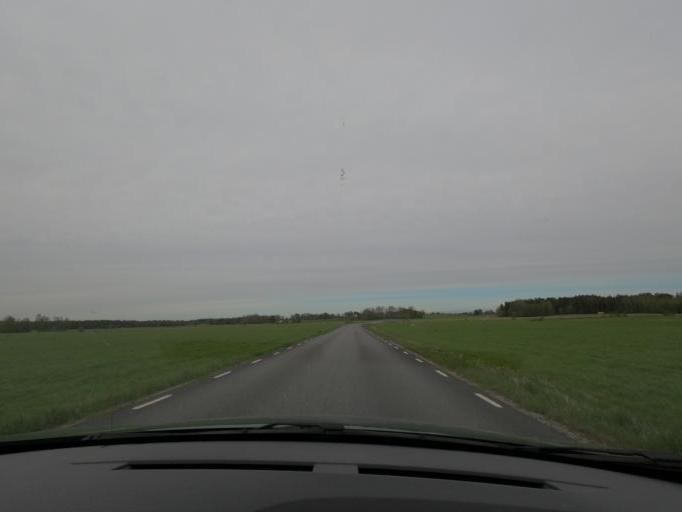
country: SE
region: Joenkoeping
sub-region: Varnamo Kommun
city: Bredaryd
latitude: 57.1284
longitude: 13.6844
